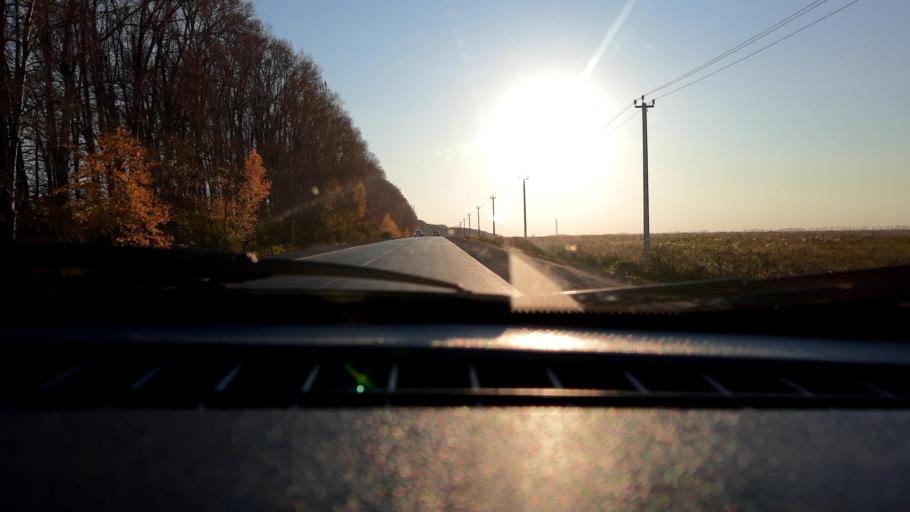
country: RU
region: Bashkortostan
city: Asanovo
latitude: 54.8225
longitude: 55.6171
